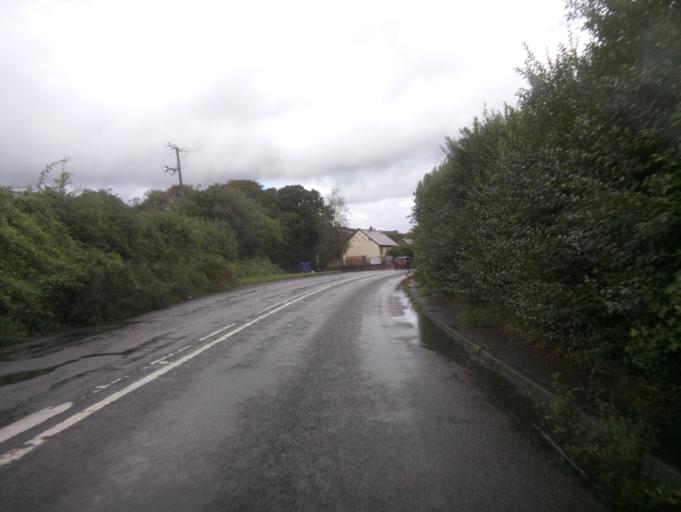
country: GB
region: England
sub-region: Devon
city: South Brent
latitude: 50.4197
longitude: -3.8367
